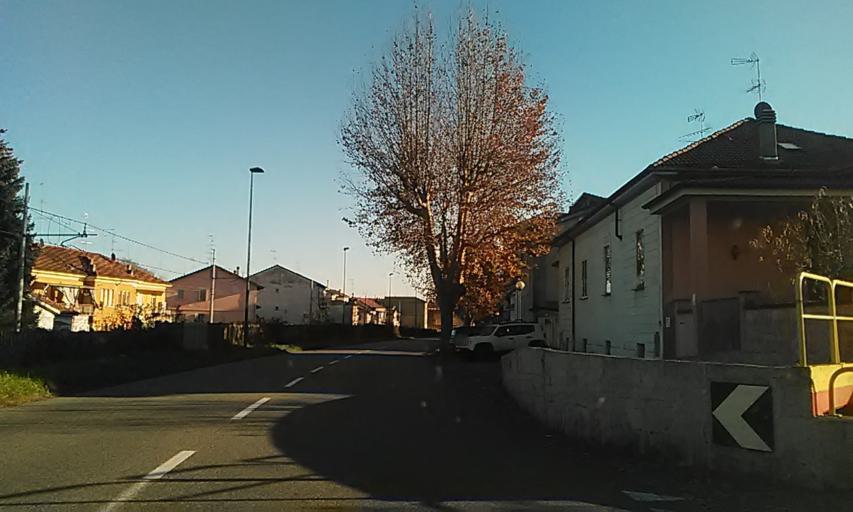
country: IT
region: Piedmont
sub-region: Provincia di Alessandria
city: Casale Monferrato
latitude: 45.1391
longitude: 8.4585
